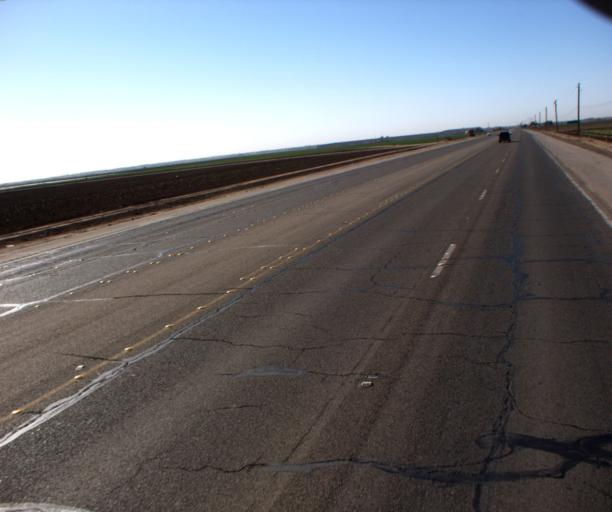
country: US
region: Arizona
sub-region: Yuma County
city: San Luis
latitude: 32.5402
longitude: -114.7869
